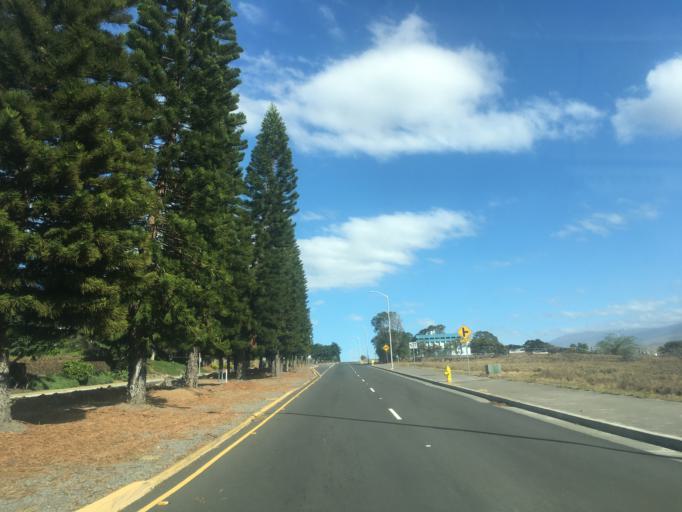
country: US
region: Hawaii
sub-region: Hawaii County
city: Waikoloa
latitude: 19.9250
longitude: -155.7962
